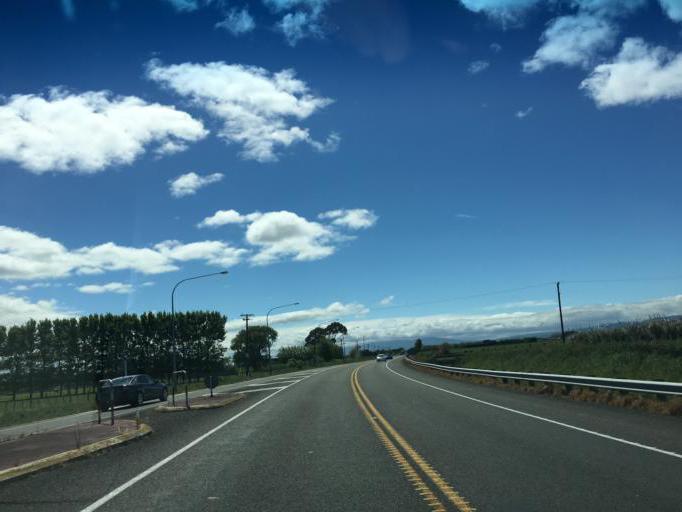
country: NZ
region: Manawatu-Wanganui
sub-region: Palmerston North City
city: Palmerston North
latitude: -40.4115
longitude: 175.4812
